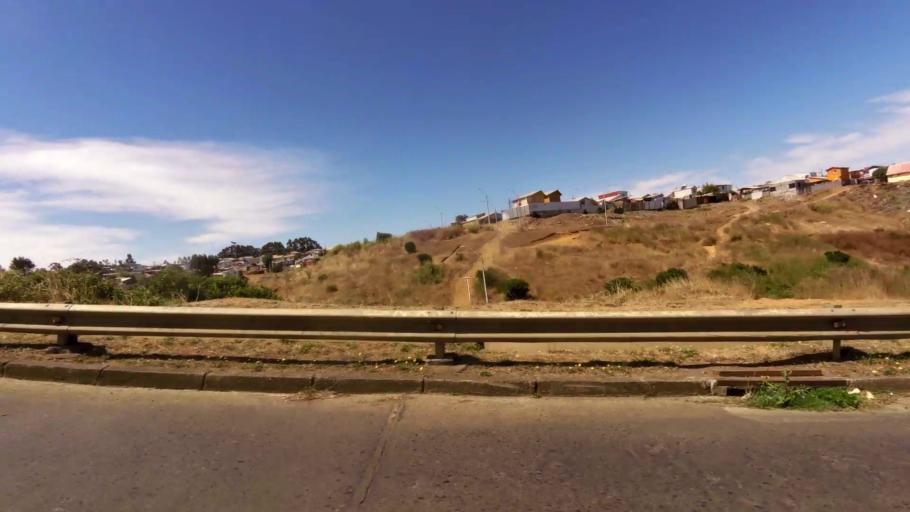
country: CL
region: Biobio
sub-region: Provincia de Concepcion
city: Talcahuano
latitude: -36.7173
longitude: -73.1421
